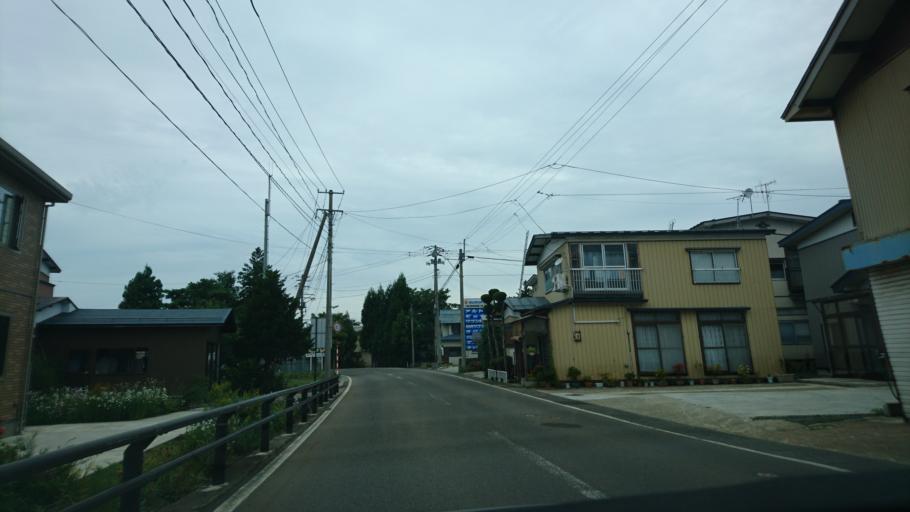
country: JP
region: Akita
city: Yuzawa
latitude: 39.1514
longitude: 140.5701
